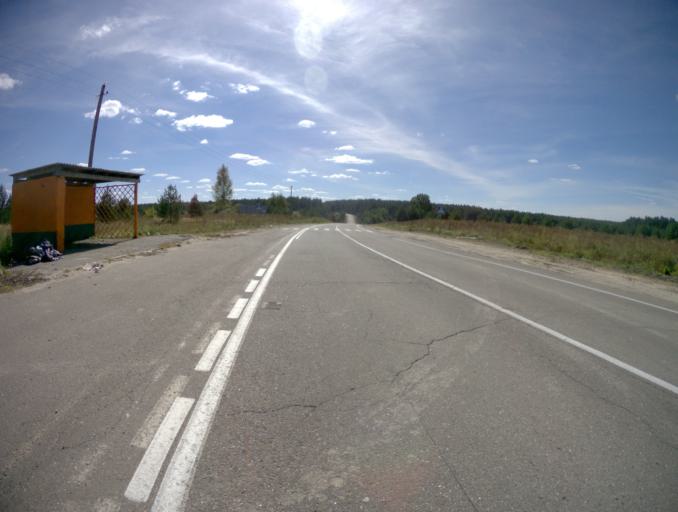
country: RU
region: Vladimir
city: Zolotkovo
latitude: 55.5924
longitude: 41.1502
